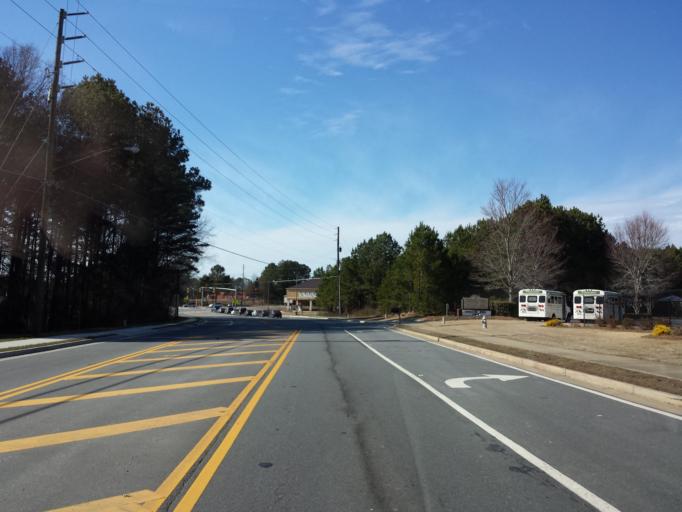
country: US
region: Georgia
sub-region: Cobb County
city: Kennesaw
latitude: 34.0284
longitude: -84.6251
